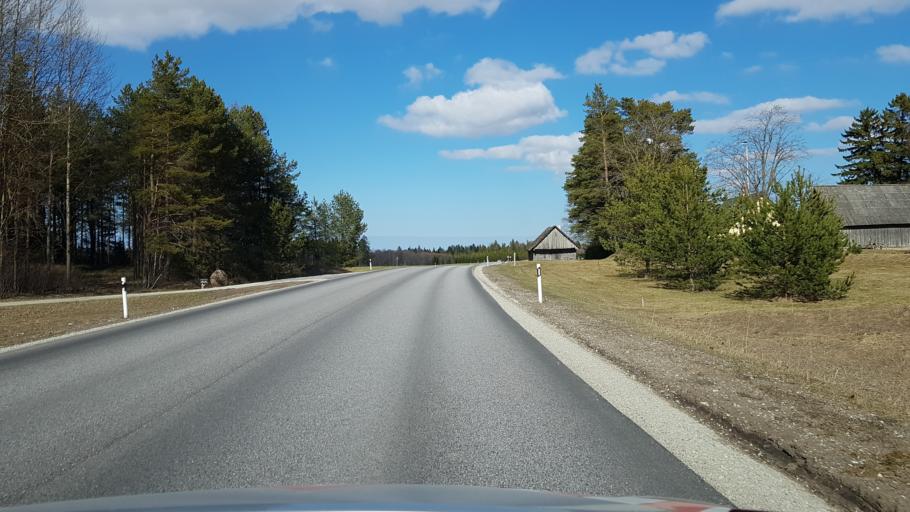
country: EE
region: Laeaene-Virumaa
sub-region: Rakvere linn
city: Rakvere
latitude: 59.2749
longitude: 26.2862
